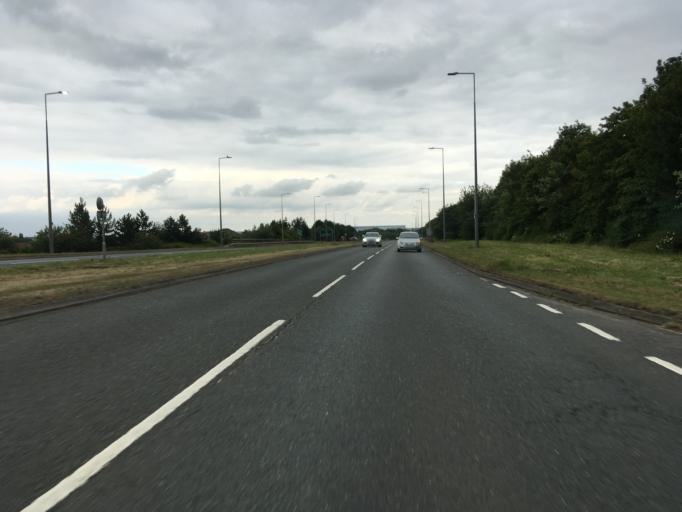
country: GB
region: England
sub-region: Milton Keynes
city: Simpson
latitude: 52.0335
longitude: -0.6977
